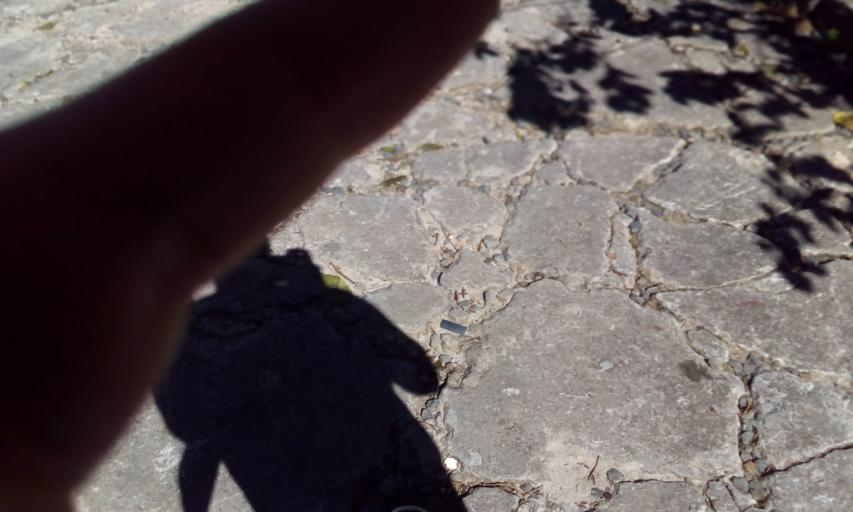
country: BR
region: Bahia
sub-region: Salvador
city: Salvador
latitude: -12.9939
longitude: -38.5206
